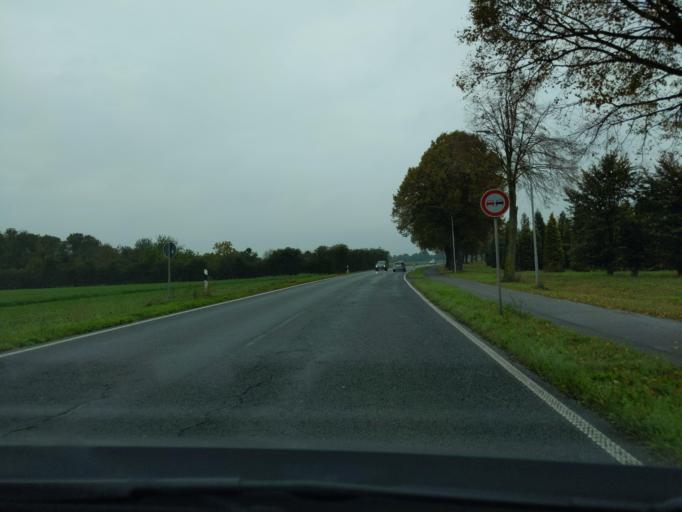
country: DE
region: North Rhine-Westphalia
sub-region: Regierungsbezirk Dusseldorf
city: Kaarst
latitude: 51.2088
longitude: 6.6084
